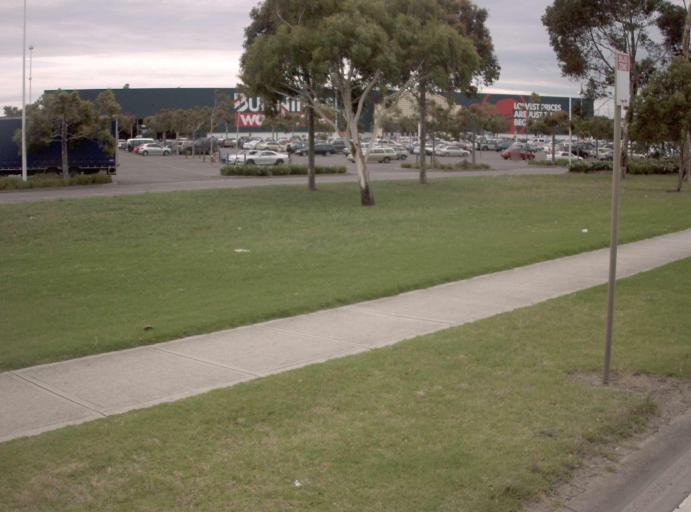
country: AU
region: Victoria
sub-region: Casey
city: Cranbourne North
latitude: -38.0827
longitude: 145.2769
